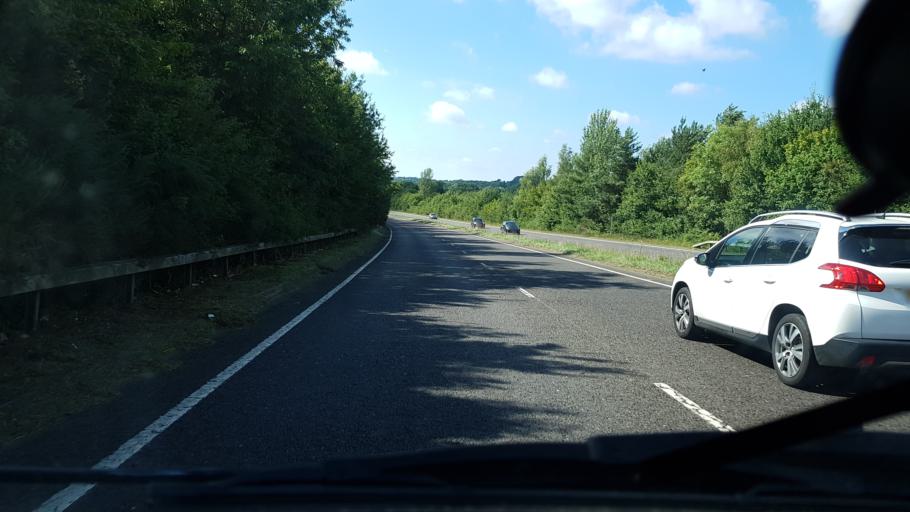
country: GB
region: England
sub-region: West Sussex
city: Horsham
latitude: 51.0857
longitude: -0.2939
